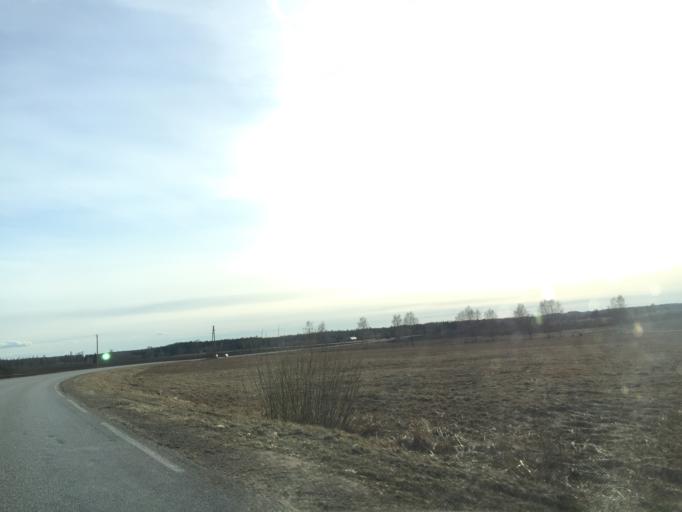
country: LV
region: Sigulda
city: Sigulda
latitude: 57.1677
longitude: 24.8115
